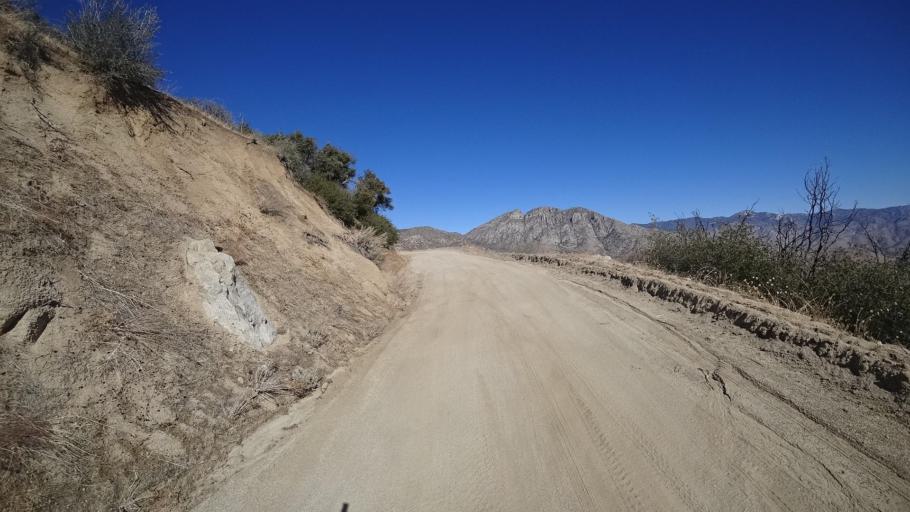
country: US
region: California
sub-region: Kern County
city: Alta Sierra
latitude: 35.7099
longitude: -118.5088
